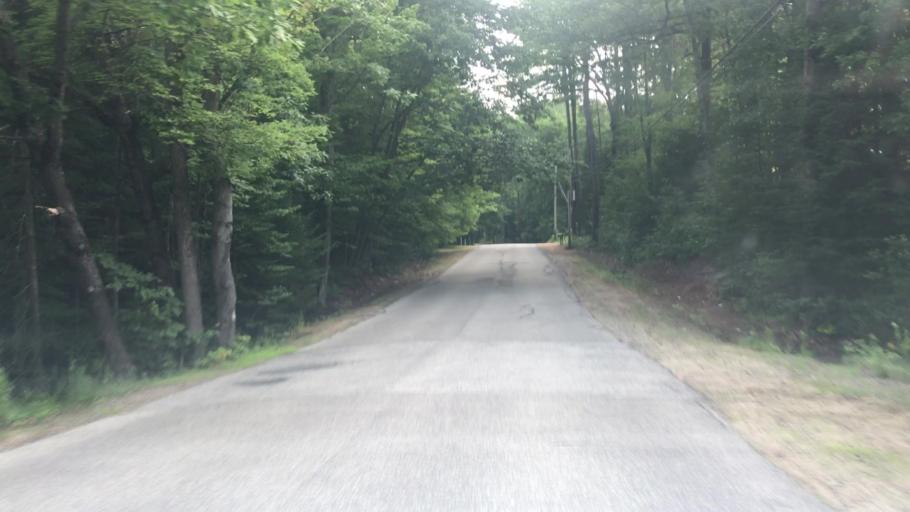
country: US
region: Maine
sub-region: Oxford County
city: South Paris
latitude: 44.2005
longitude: -70.5156
